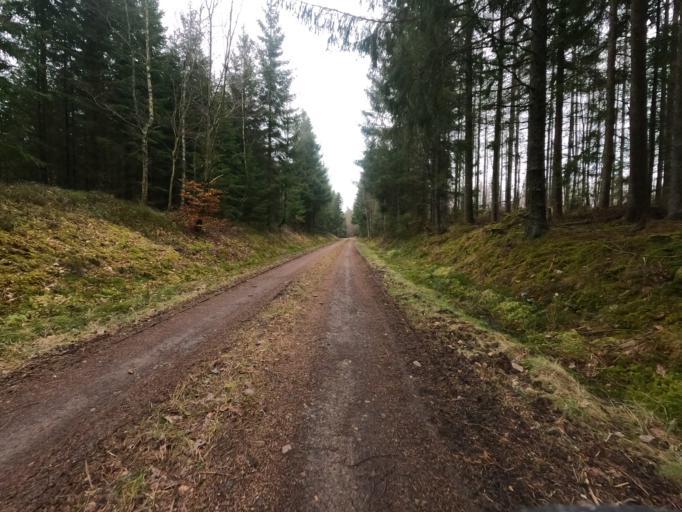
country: SE
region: Kronoberg
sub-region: Markaryds Kommun
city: Stromsnasbruk
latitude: 56.7902
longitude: 13.6284
